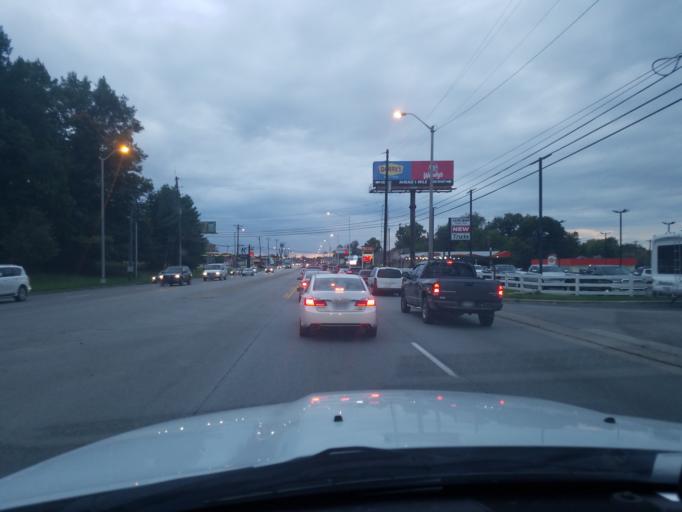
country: US
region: Kentucky
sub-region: Henderson County
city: Henderson
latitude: 37.8812
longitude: -87.5646
